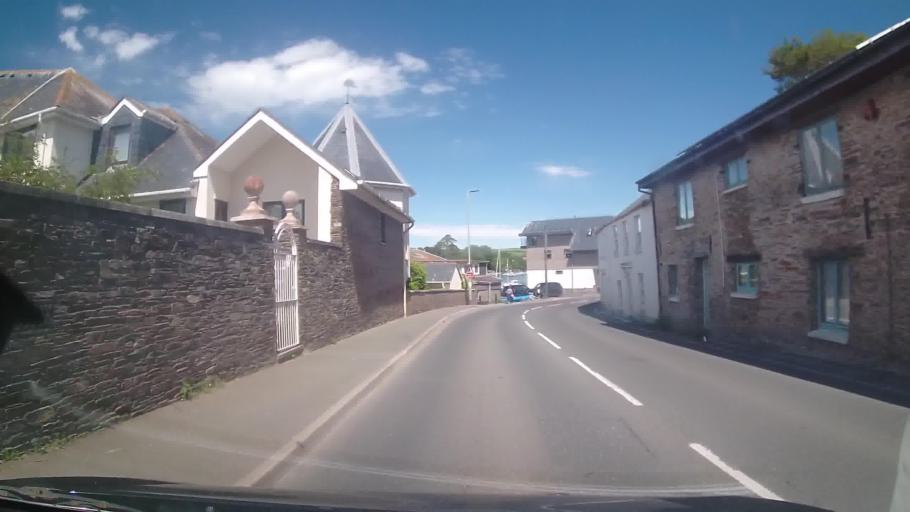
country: GB
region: England
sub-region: Devon
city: Kingsbridge
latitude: 50.2759
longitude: -3.7720
